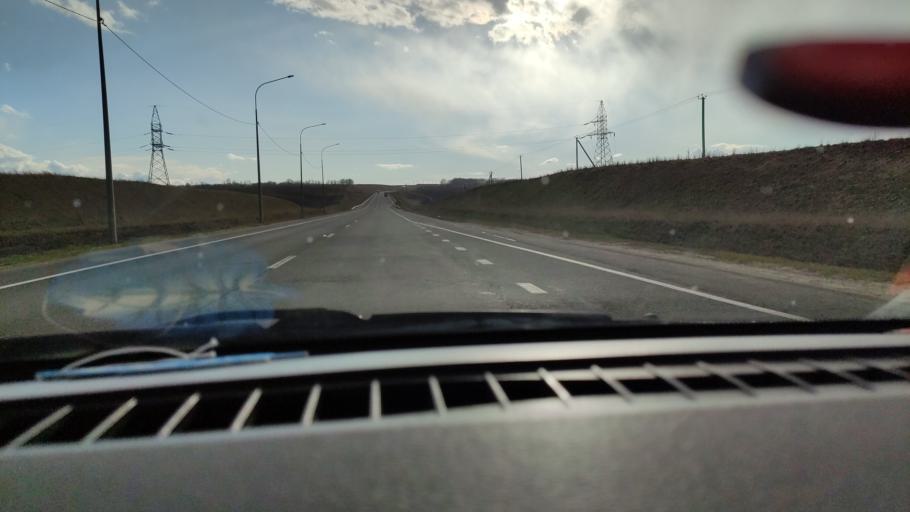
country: RU
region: Saratov
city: Yelshanka
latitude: 51.8224
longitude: 46.3764
